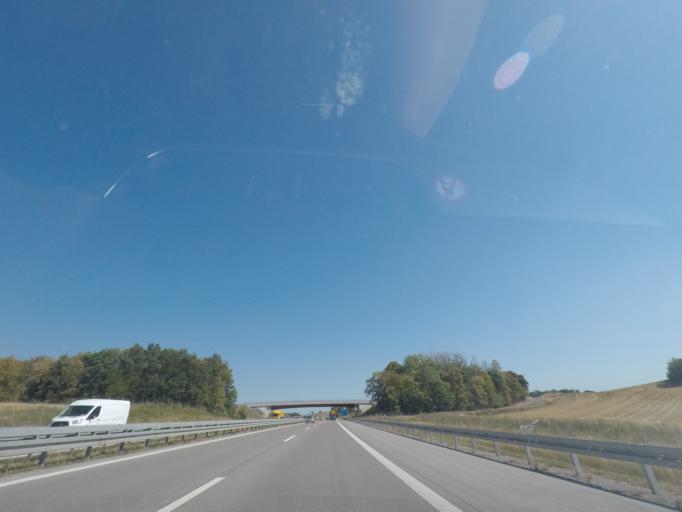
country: DE
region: Saxony
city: Moritzburg
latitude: 51.1498
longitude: 13.7474
